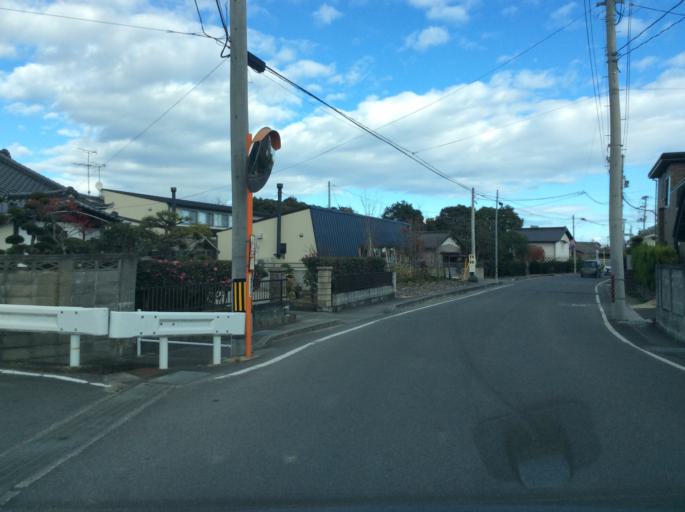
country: JP
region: Fukushima
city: Iwaki
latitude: 37.0763
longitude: 140.9517
